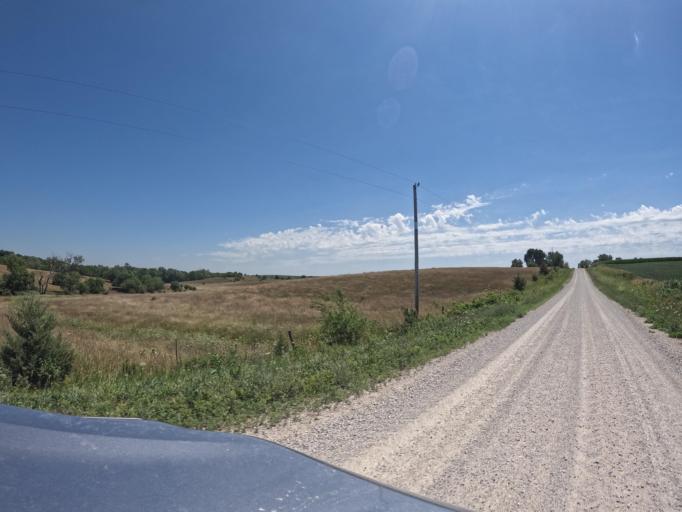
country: US
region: Iowa
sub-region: Keokuk County
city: Sigourney
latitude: 41.4177
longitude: -92.3164
